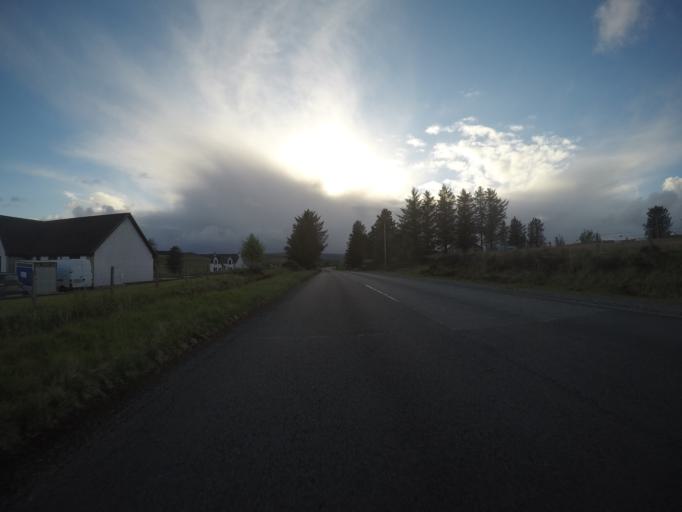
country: GB
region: Scotland
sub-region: Highland
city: Isle of Skye
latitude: 57.4512
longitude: -6.2844
